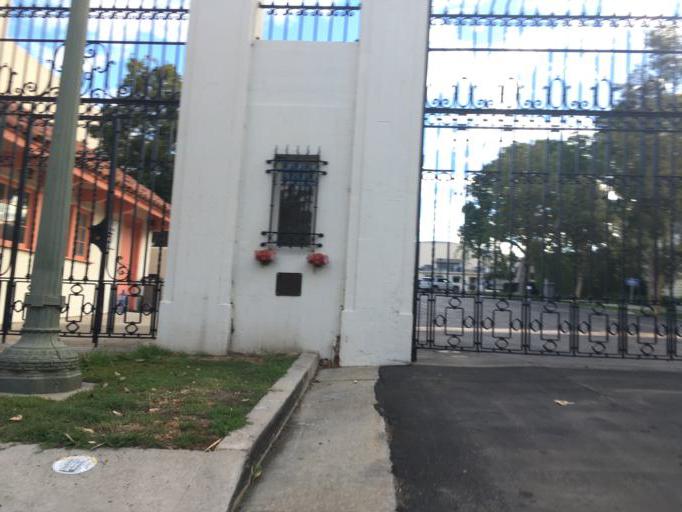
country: US
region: California
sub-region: Los Angeles County
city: Century City
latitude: 34.0510
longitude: -118.4147
